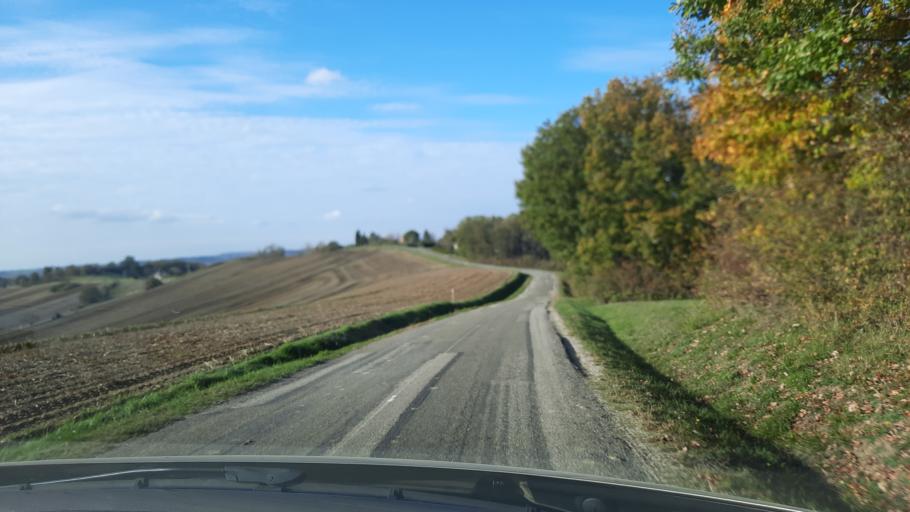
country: FR
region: Midi-Pyrenees
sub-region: Departement du Tarn-et-Garonne
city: Lafrancaise
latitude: 44.1491
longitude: 1.2959
